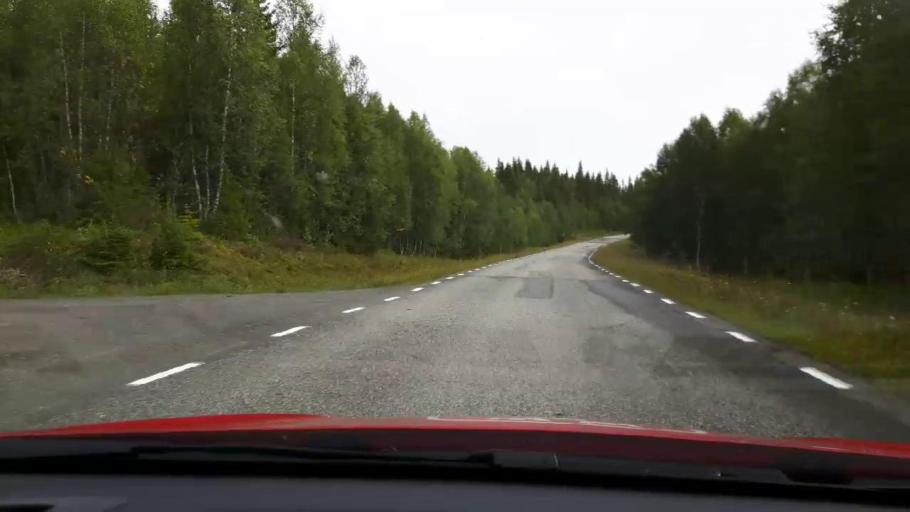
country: SE
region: Jaemtland
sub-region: Are Kommun
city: Are
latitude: 63.7393
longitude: 13.0382
